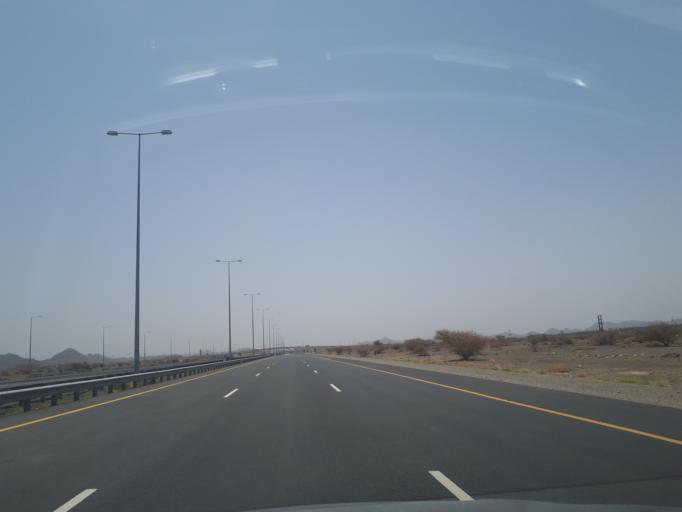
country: OM
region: Ash Sharqiyah
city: Ibra'
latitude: 22.7768
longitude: 58.5146
